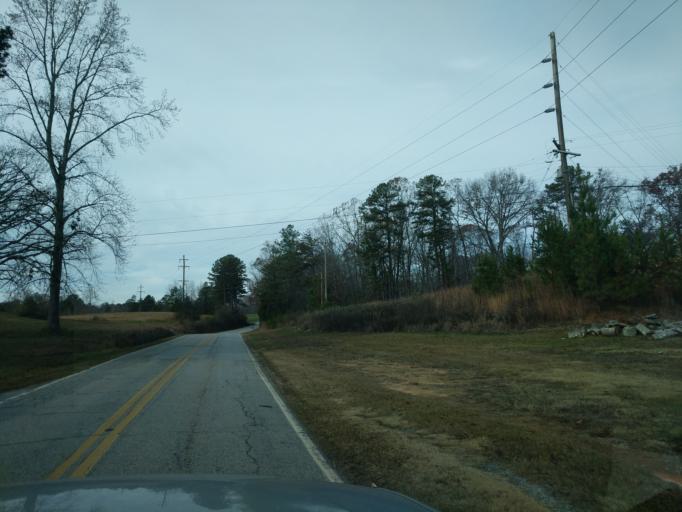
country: US
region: South Carolina
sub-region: Oconee County
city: Walhalla
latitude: 34.8290
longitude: -83.0457
